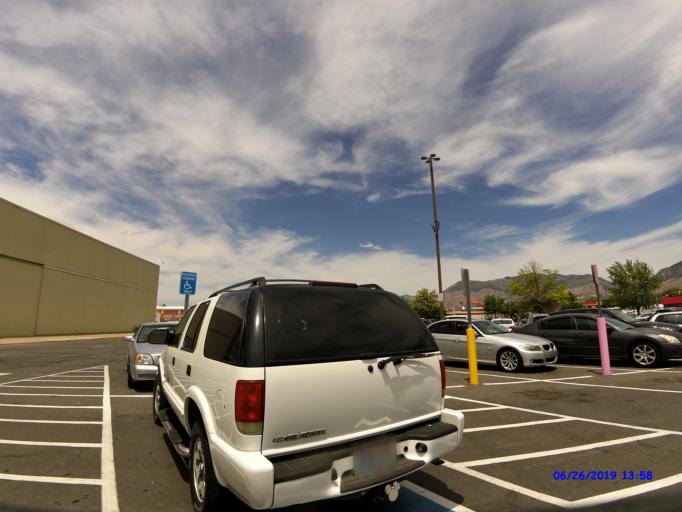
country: US
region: Utah
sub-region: Weber County
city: South Ogden
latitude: 41.1973
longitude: -111.9809
